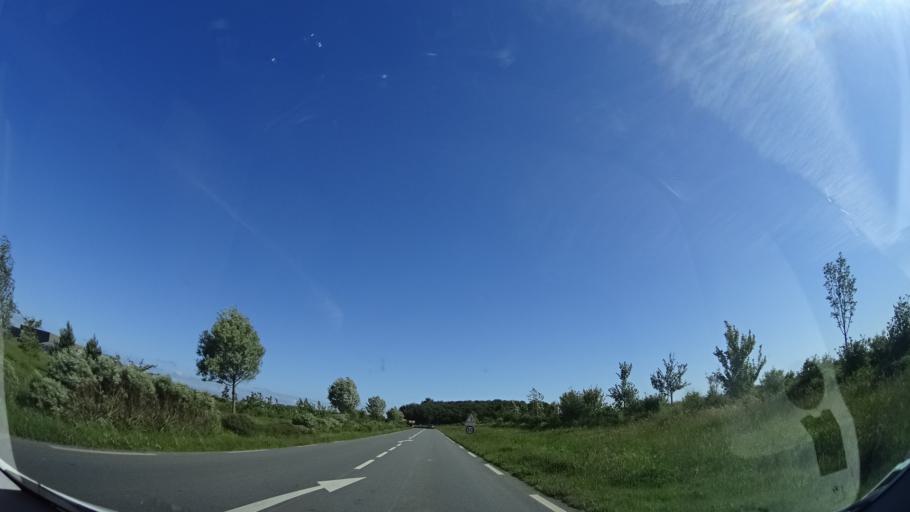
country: FR
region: Brittany
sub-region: Departement d'Ille-et-Vilaine
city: Saint-Jouan-des-Guerets
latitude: 48.6095
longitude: -1.9708
